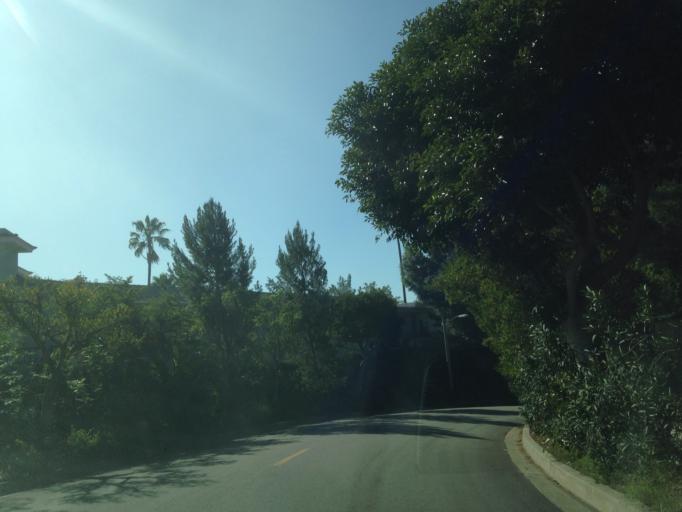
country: US
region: California
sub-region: Los Angeles County
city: Beverly Hills
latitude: 34.1005
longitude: -118.3924
